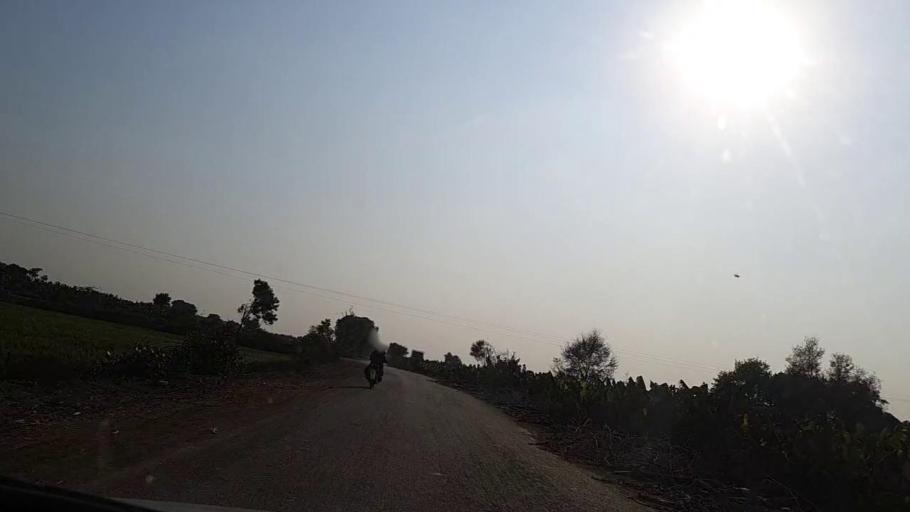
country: PK
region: Sindh
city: Sakrand
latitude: 26.0767
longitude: 68.2638
